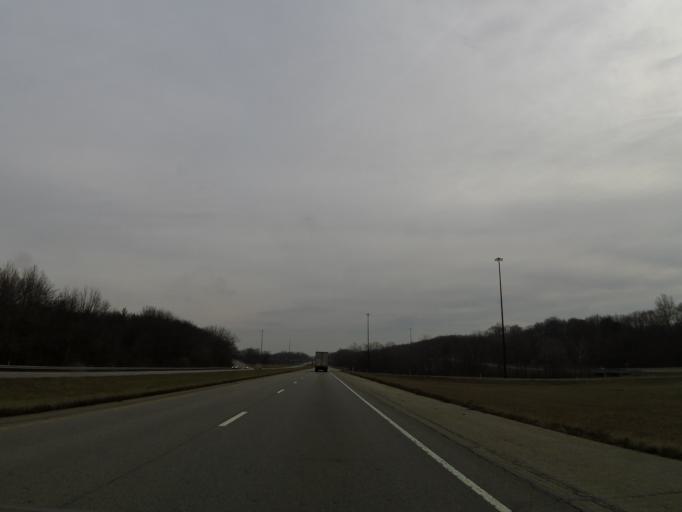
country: US
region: Indiana
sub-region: Fountain County
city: Covington
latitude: 40.1197
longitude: -87.4591
